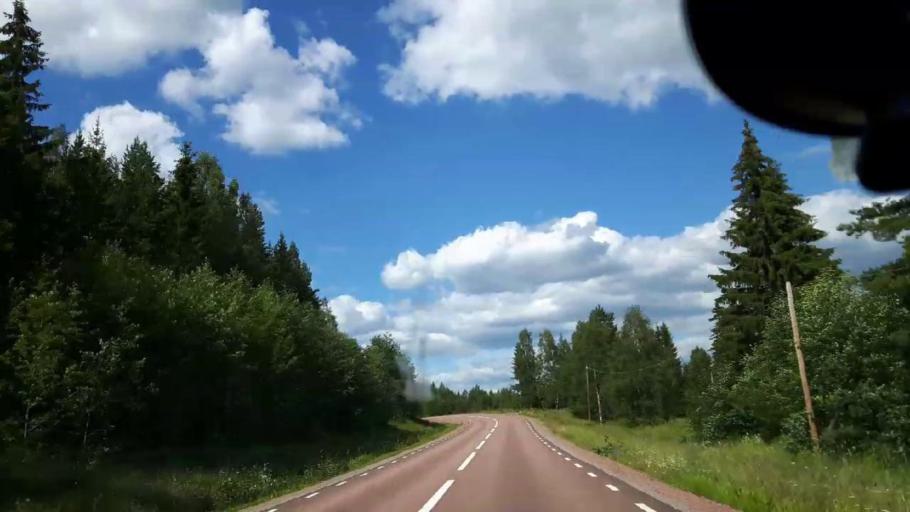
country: SE
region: Jaemtland
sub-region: Ragunda Kommun
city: Hammarstrand
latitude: 63.0232
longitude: 16.5399
